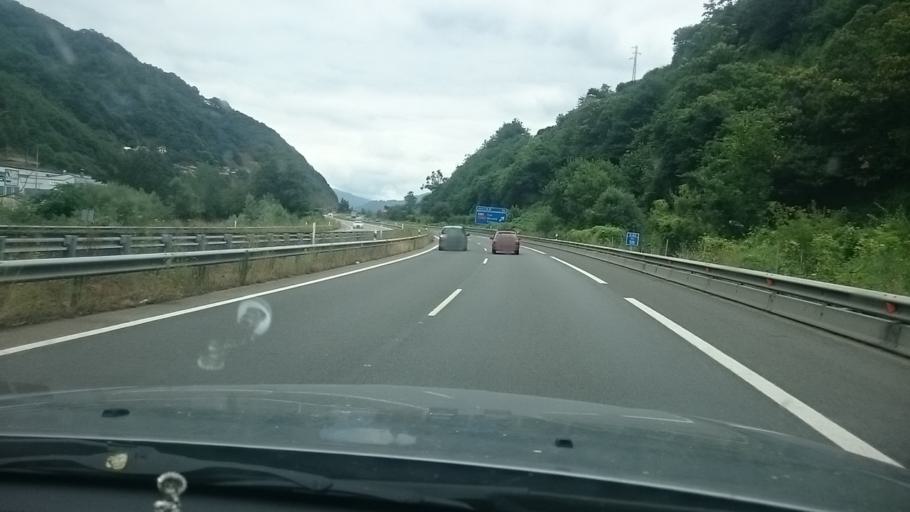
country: ES
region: Asturias
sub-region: Province of Asturias
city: Pola de Lena
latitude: 43.1893
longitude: -5.7927
